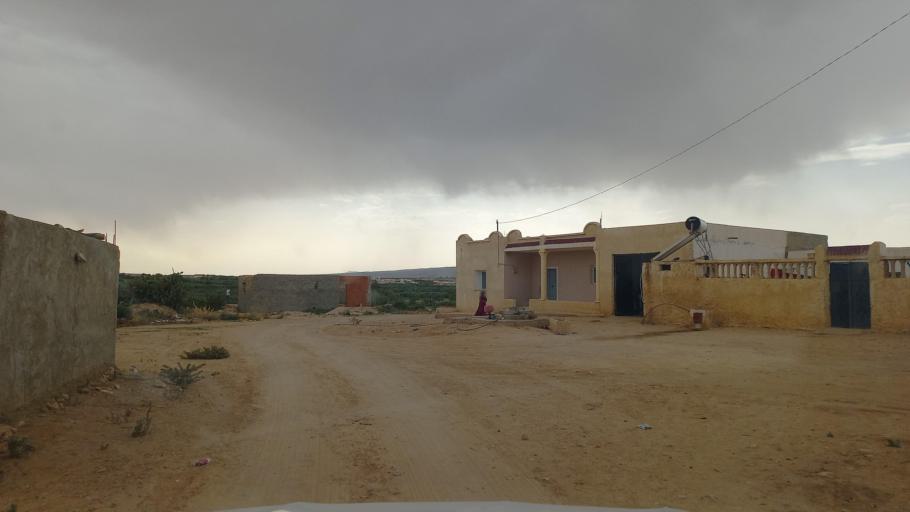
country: TN
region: Al Qasrayn
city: Sbiba
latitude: 35.3838
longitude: 9.0629
